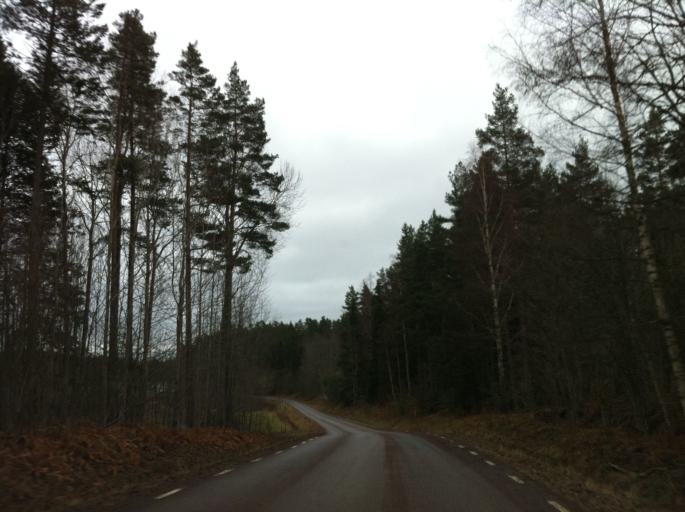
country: SE
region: Kalmar
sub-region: Vasterviks Kommun
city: Vaestervik
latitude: 57.9024
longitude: 16.6767
